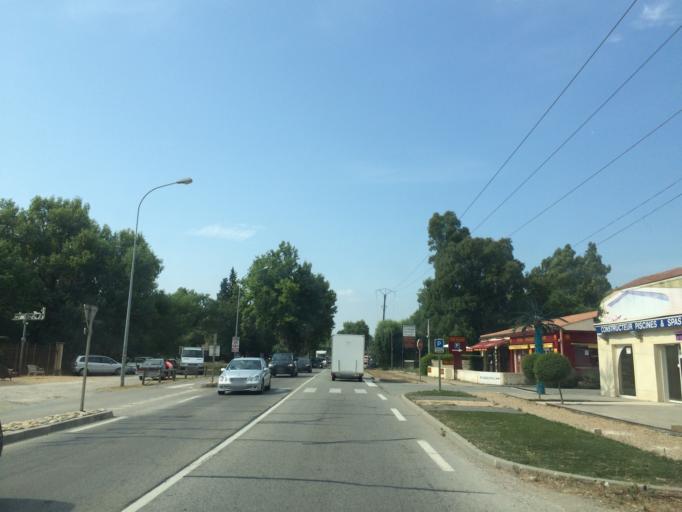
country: FR
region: Provence-Alpes-Cote d'Azur
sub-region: Departement du Var
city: Gassin
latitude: 43.2767
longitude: 6.5754
